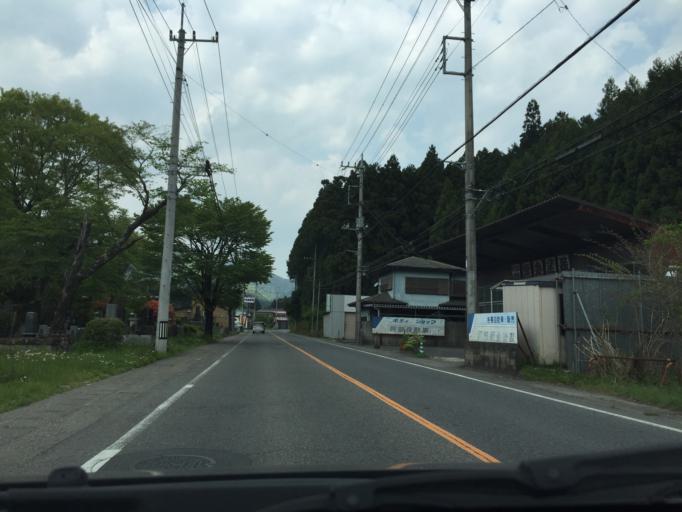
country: JP
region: Tochigi
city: Imaichi
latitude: 36.7887
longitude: 139.7063
